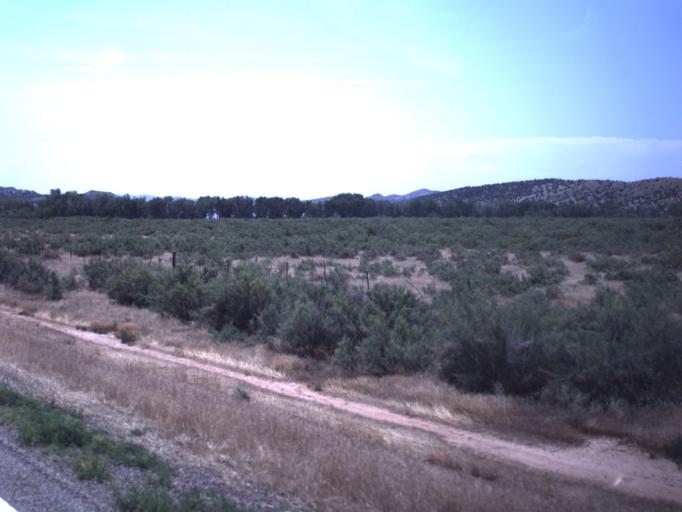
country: US
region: Utah
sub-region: Uintah County
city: Vernal
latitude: 40.5378
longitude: -109.5236
